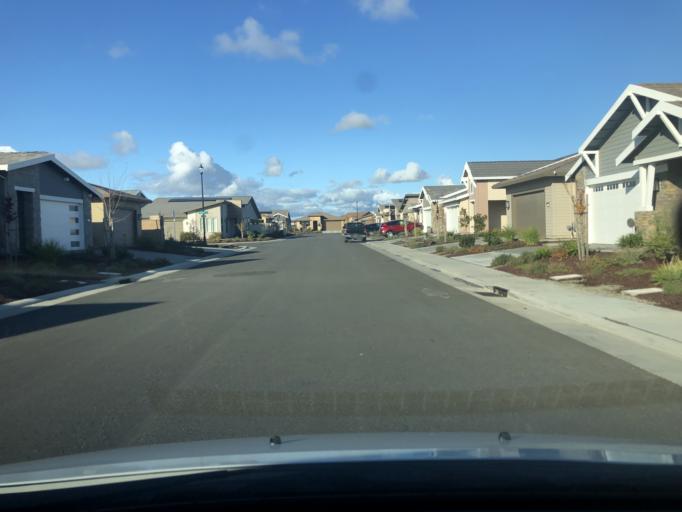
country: US
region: California
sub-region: Sacramento County
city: Antelope
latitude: 38.7735
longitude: -121.3881
